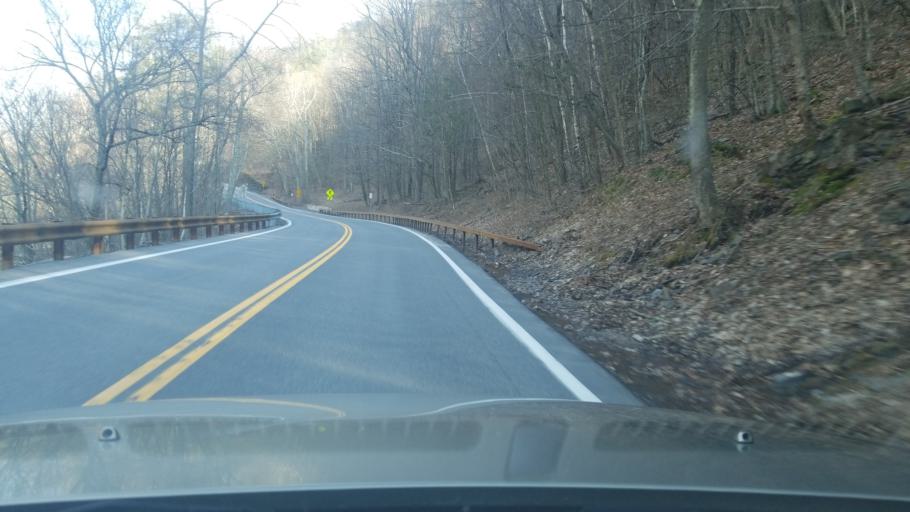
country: US
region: New York
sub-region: Greene County
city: Palenville
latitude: 42.1771
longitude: -74.0484
